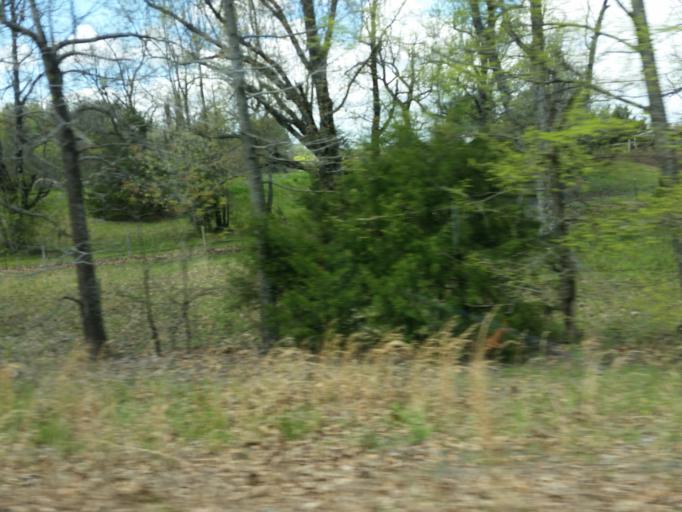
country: US
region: Arkansas
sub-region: Craighead County
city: Brookland
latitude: 36.0311
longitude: -90.6799
